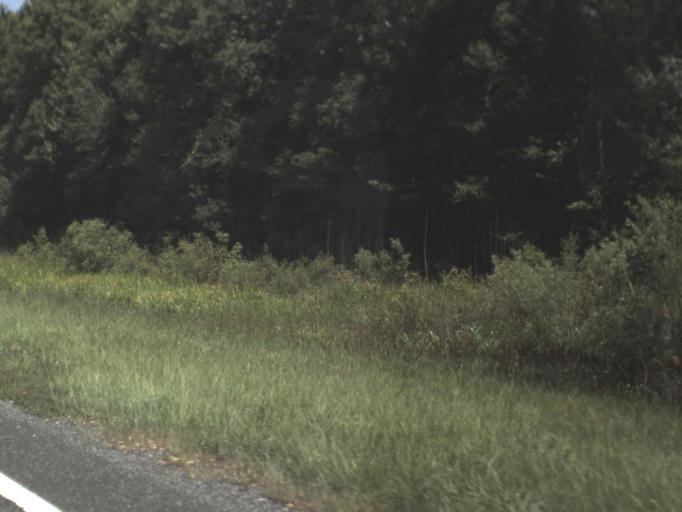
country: US
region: Florida
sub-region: Dixie County
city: Cross City
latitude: 29.6709
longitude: -83.2290
